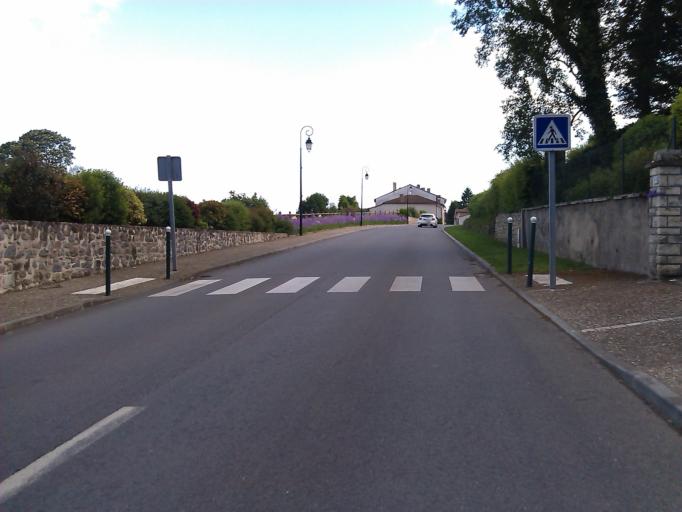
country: FR
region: Poitou-Charentes
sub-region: Departement de la Vienne
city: Availles-Limouzine
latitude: 46.2328
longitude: 0.6766
